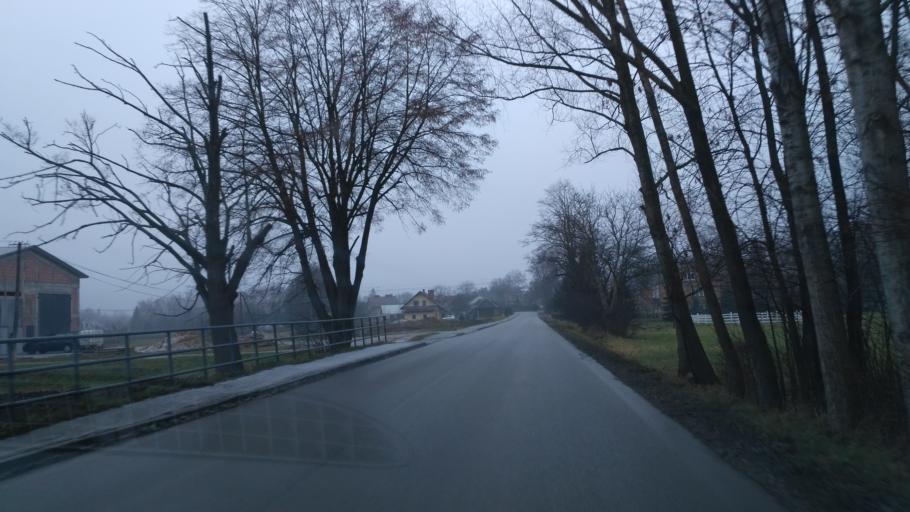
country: PL
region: Subcarpathian Voivodeship
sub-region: Powiat lancucki
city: Markowa
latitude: 50.0267
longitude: 22.3411
